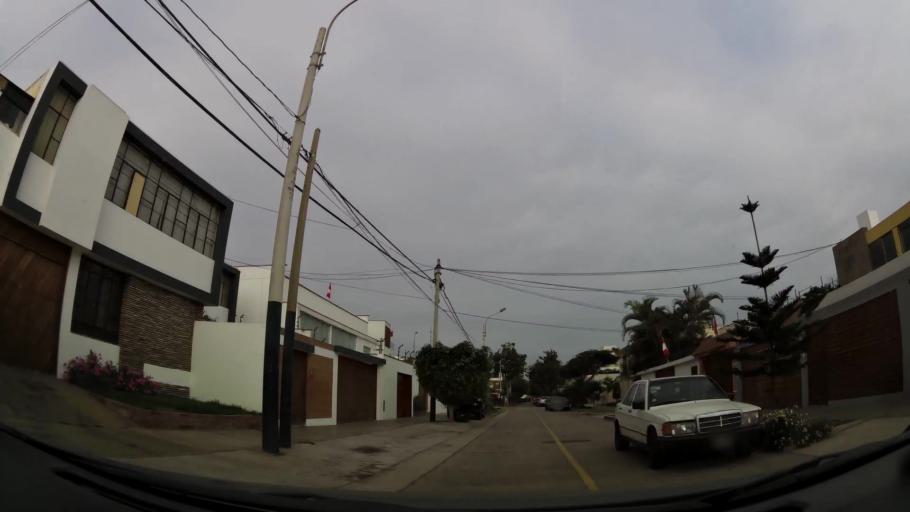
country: PE
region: Lima
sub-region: Lima
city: San Isidro
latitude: -12.1051
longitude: -77.0575
